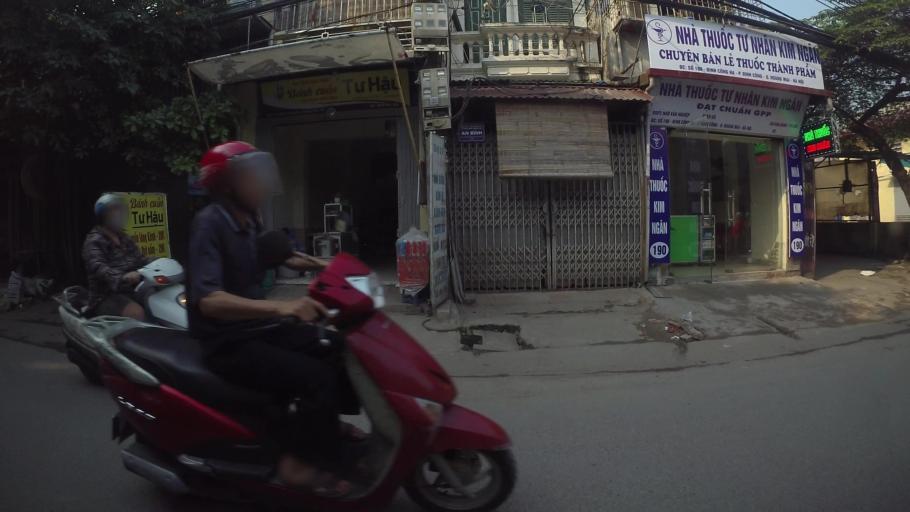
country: VN
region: Ha Noi
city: Thanh Xuan
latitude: 20.9838
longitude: 105.8250
